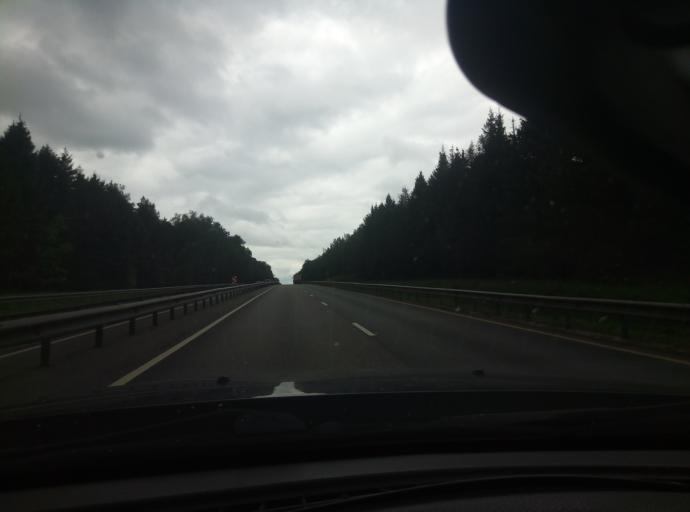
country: RU
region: Kaluga
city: Maloyaroslavets
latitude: 54.9908
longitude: 36.5121
